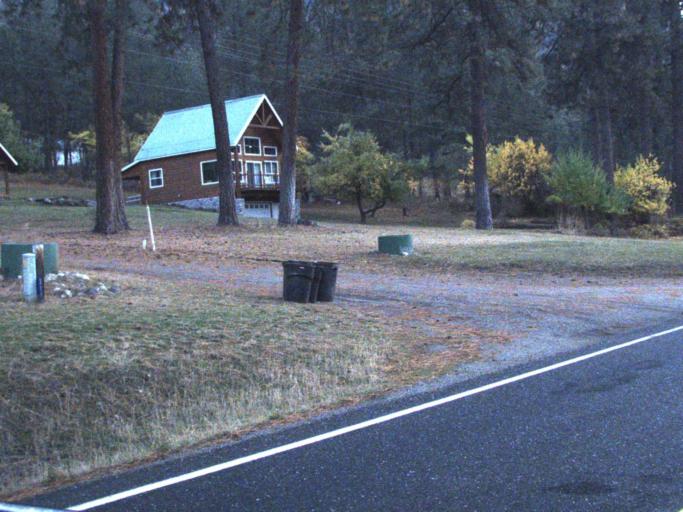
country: US
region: Washington
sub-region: Stevens County
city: Kettle Falls
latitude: 48.2526
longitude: -118.1348
